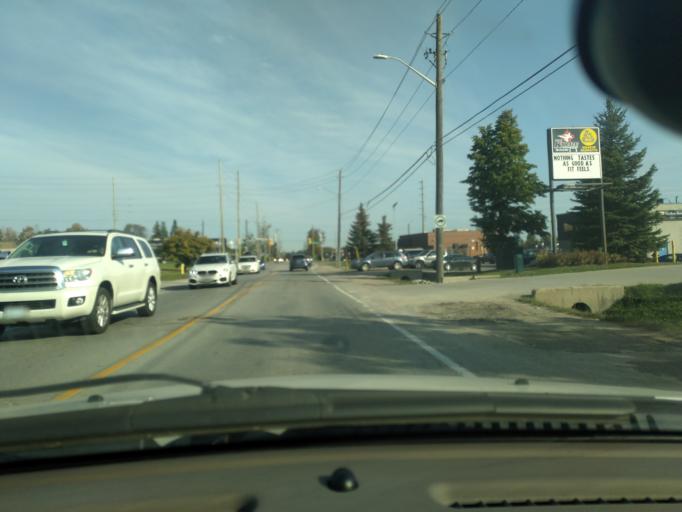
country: CA
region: Ontario
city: Barrie
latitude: 44.3520
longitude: -79.6647
